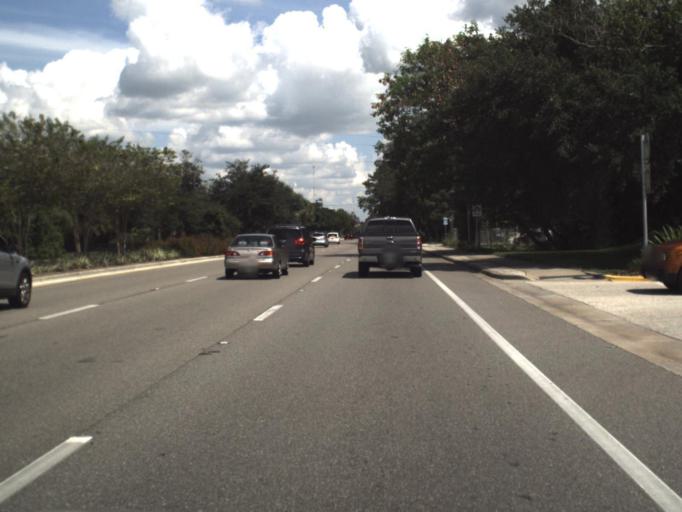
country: US
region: Florida
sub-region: Sarasota County
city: Kensington Park
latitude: 27.3374
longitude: -82.4856
